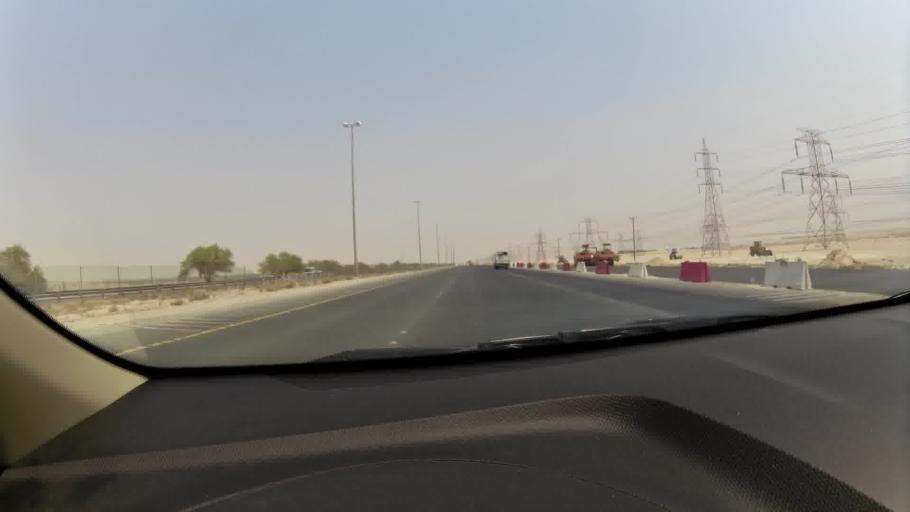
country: KW
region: Al Farwaniyah
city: Al Farwaniyah
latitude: 29.1834
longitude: 47.9073
